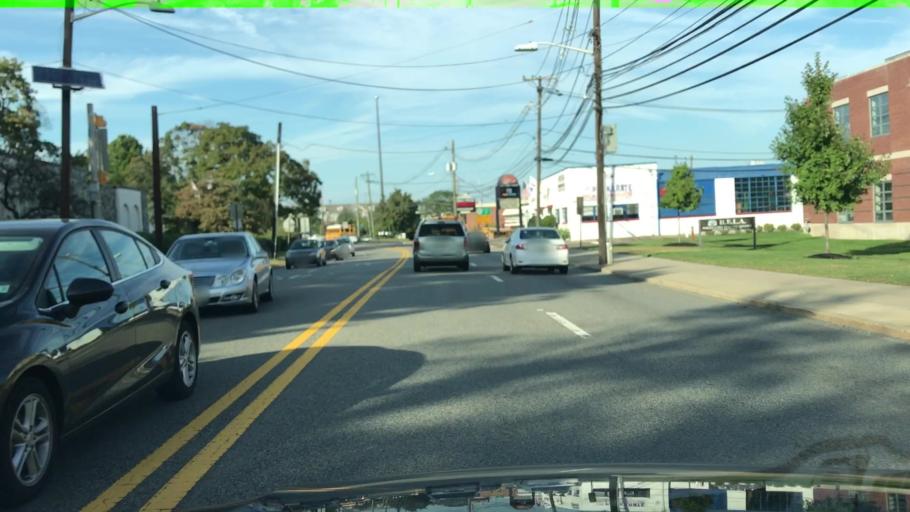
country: US
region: New Jersey
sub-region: Bergen County
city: Teaneck
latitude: 40.9036
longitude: -74.0339
